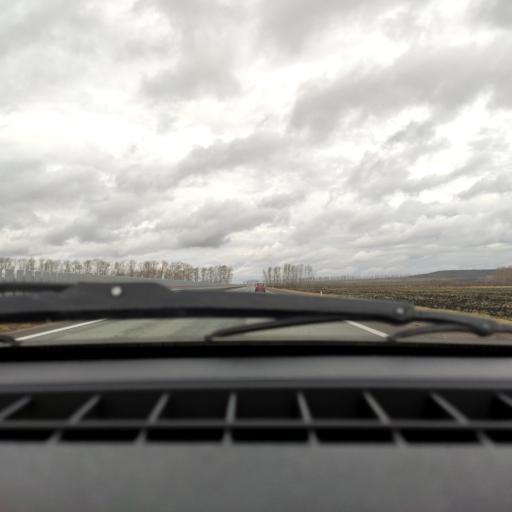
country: RU
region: Bashkortostan
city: Asanovo
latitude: 54.9439
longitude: 55.5817
